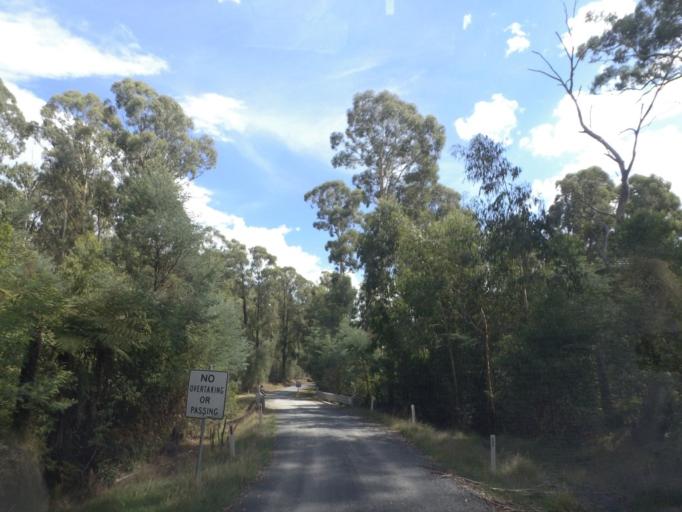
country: AU
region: Victoria
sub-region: Murrindindi
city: Alexandra
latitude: -37.4483
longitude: 145.7553
